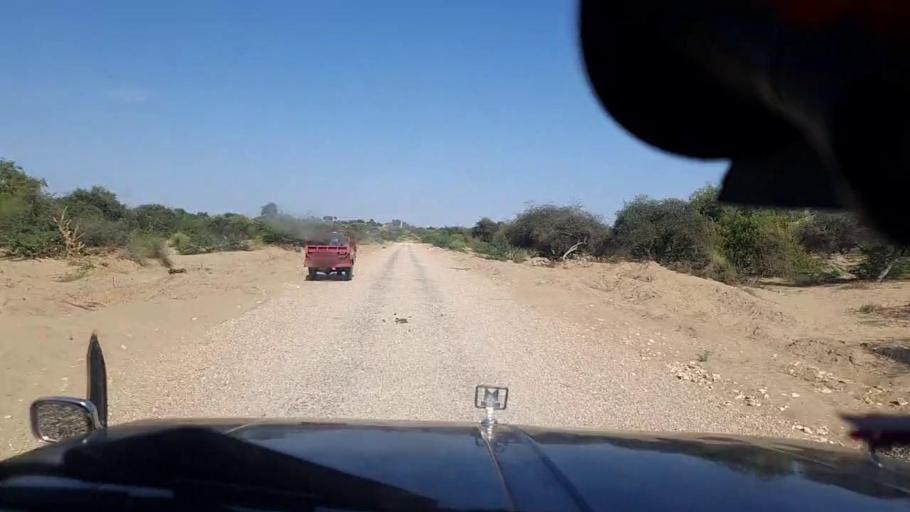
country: PK
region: Sindh
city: Diplo
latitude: 24.4692
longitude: 69.7991
